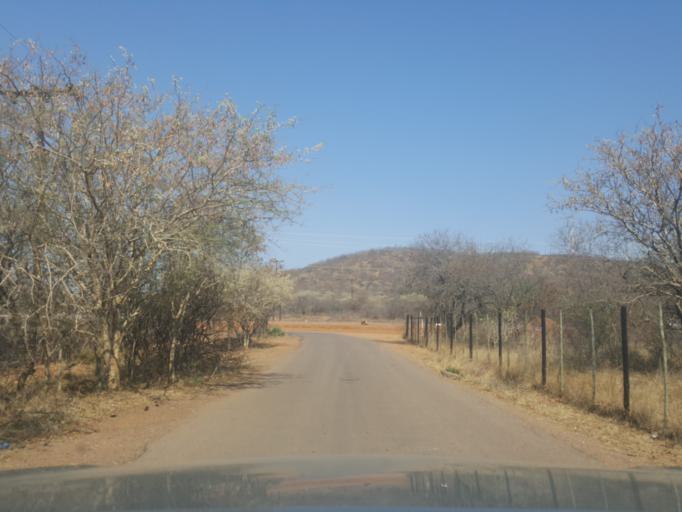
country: BW
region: Kweneng
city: Gabane
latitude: -24.7449
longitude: 25.8297
